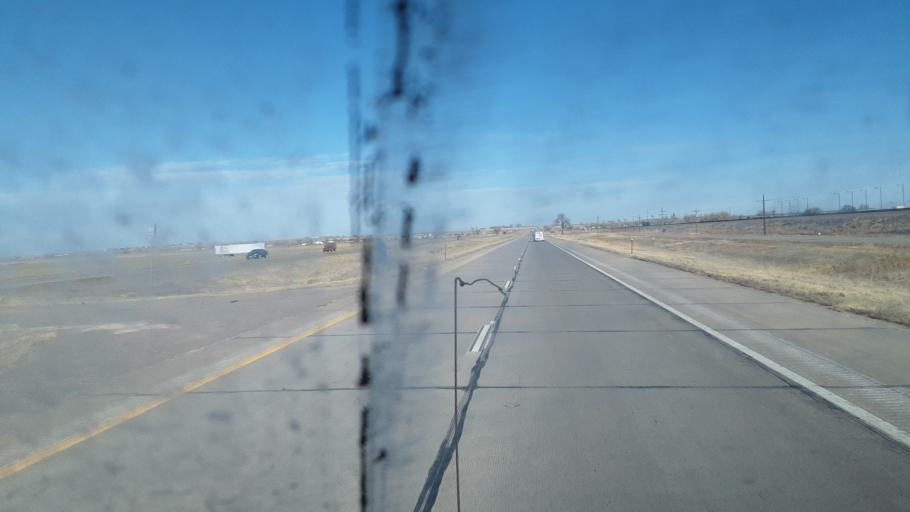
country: US
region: Colorado
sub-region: Weld County
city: Hudson
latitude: 40.0895
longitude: -104.6203
